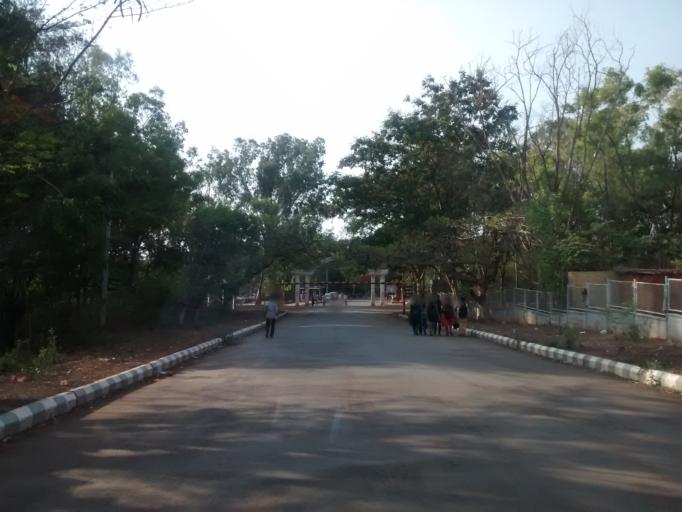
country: IN
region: Karnataka
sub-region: Dharwad
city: Hubli
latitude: 15.4444
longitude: 74.9829
